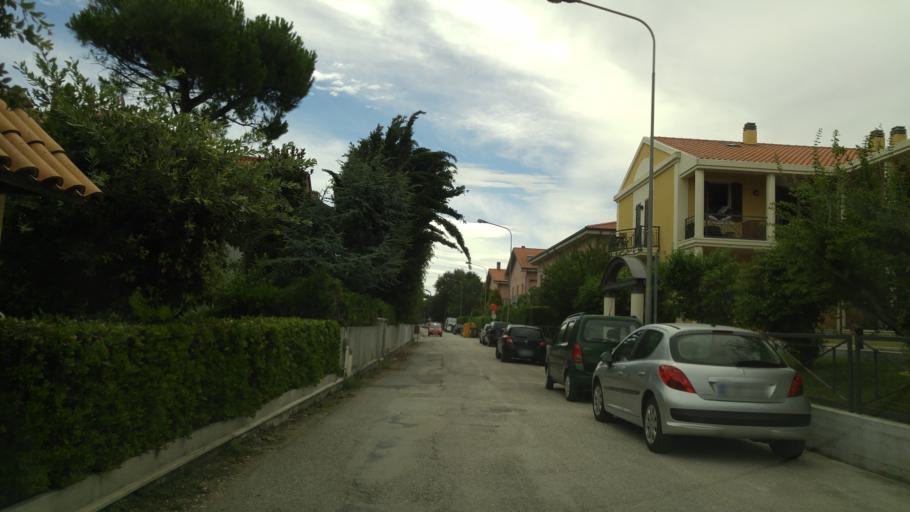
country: IT
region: The Marches
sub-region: Provincia di Pesaro e Urbino
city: Centinarola
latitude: 43.8605
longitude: 12.9901
